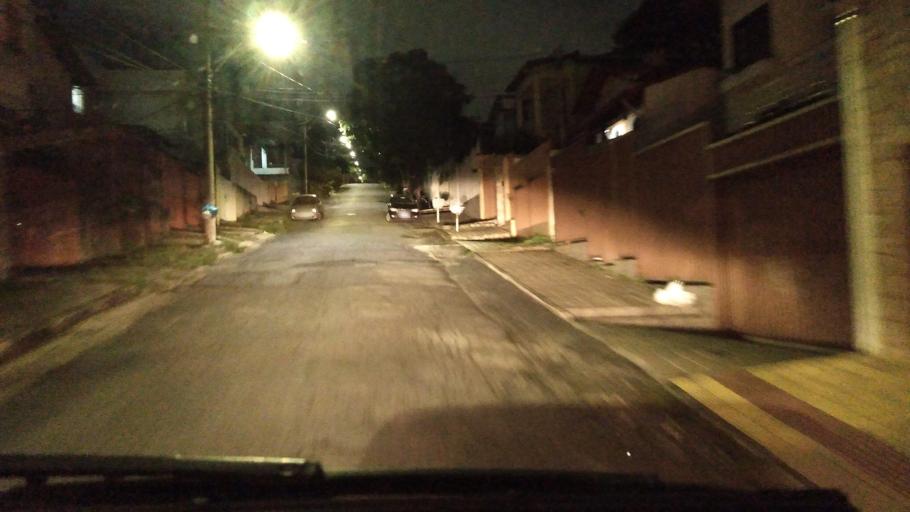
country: BR
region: Minas Gerais
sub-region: Belo Horizonte
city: Belo Horizonte
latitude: -19.8926
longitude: -43.9719
